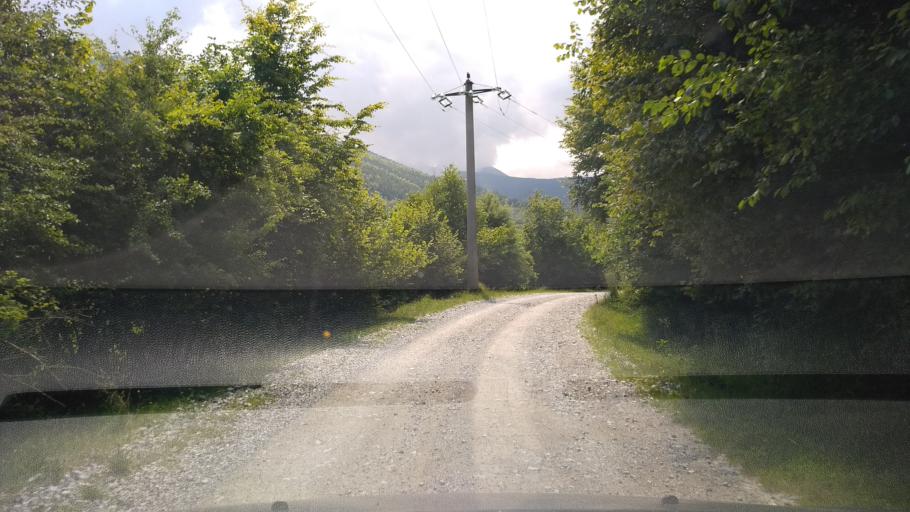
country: RO
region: Hunedoara
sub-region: Comuna Rau de Mori
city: Rau de Mori
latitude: 45.4508
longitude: 22.8957
